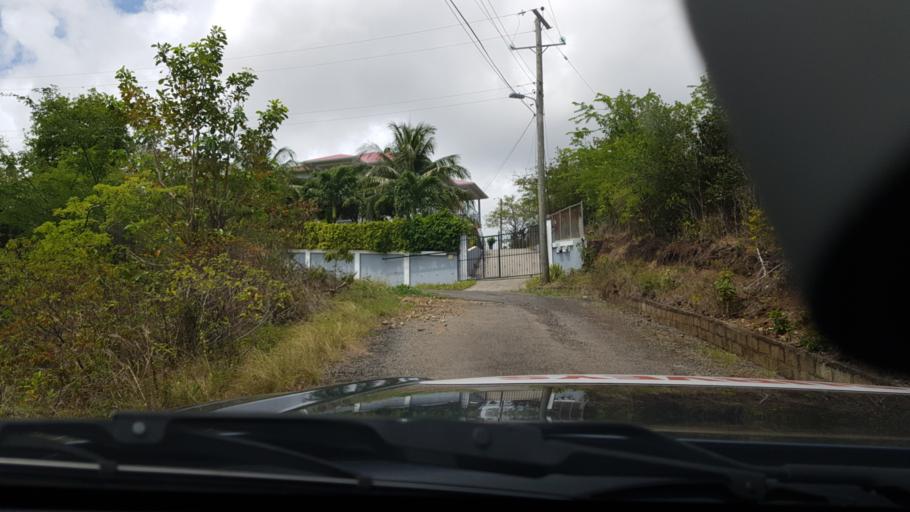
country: LC
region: Gros-Islet
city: Gros Islet
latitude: 14.0676
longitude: -60.9295
